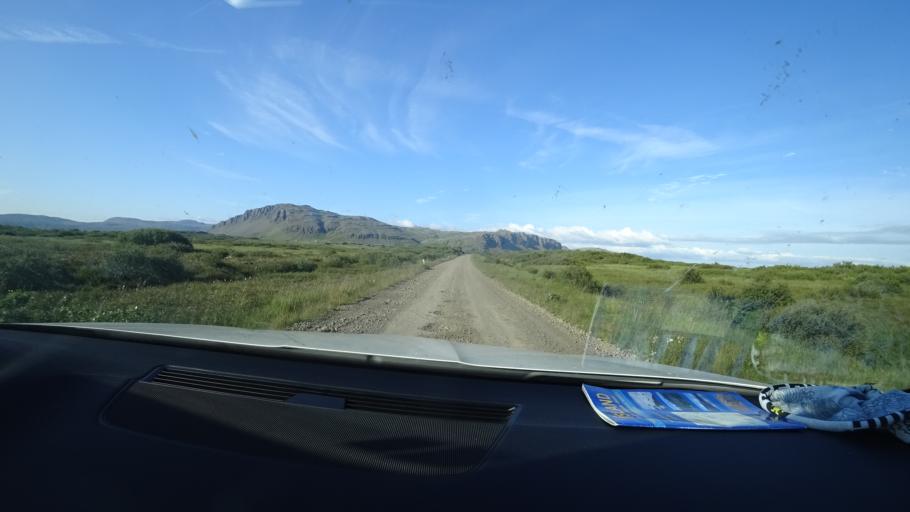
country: IS
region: West
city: Borgarnes
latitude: 64.6813
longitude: -21.9522
